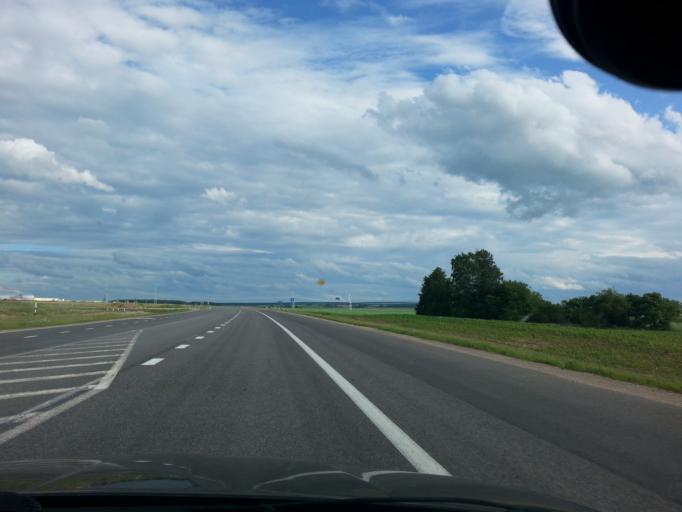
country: BY
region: Grodnenskaya
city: Astravyets
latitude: 54.7648
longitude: 26.0650
